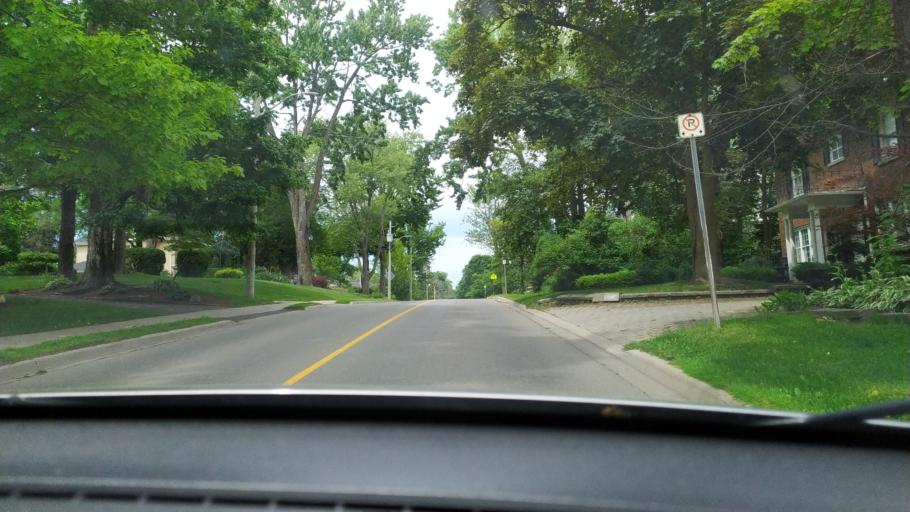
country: CA
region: Ontario
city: Stratford
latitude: 43.3720
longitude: -80.9939
